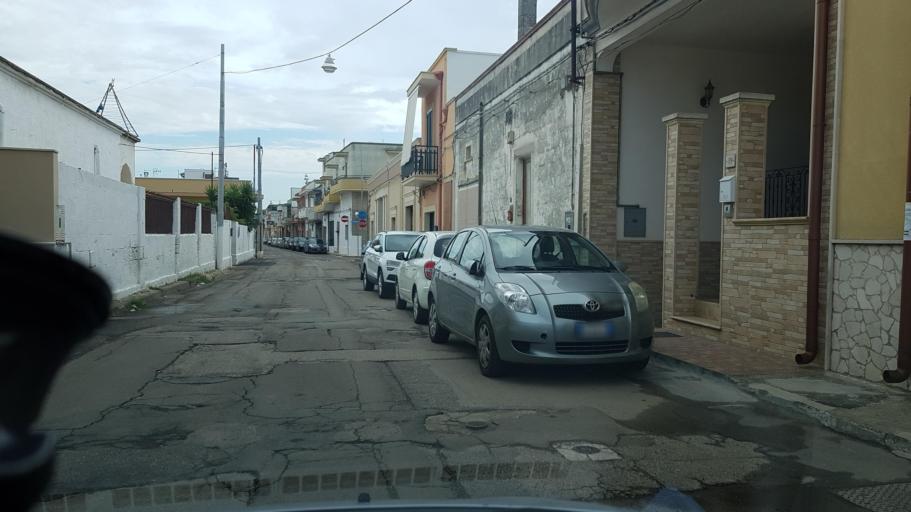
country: IT
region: Apulia
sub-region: Provincia di Brindisi
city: Torre Santa Susanna
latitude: 40.4716
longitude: 17.7408
